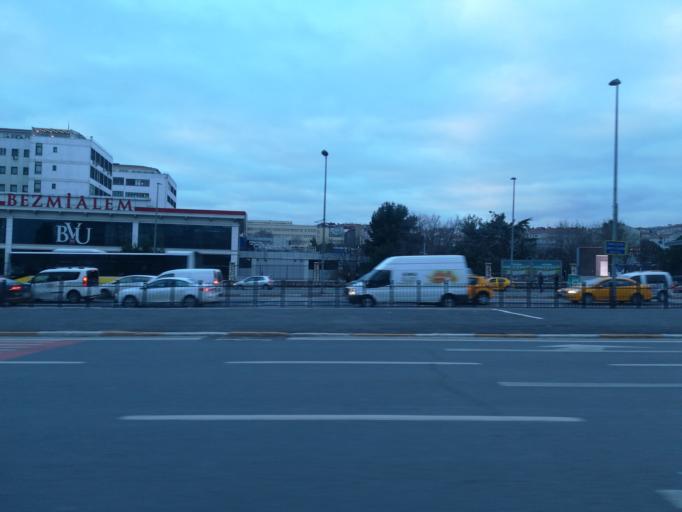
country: TR
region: Istanbul
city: Istanbul
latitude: 41.0205
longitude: 28.9353
